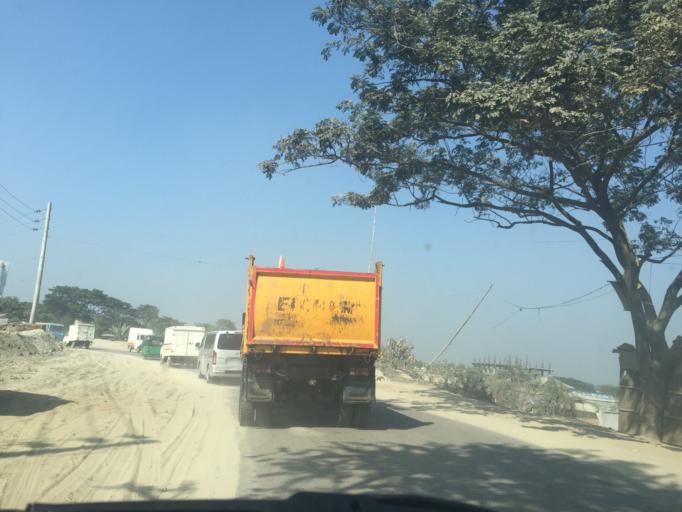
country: BD
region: Dhaka
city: Tungi
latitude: 23.8285
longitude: 90.3450
